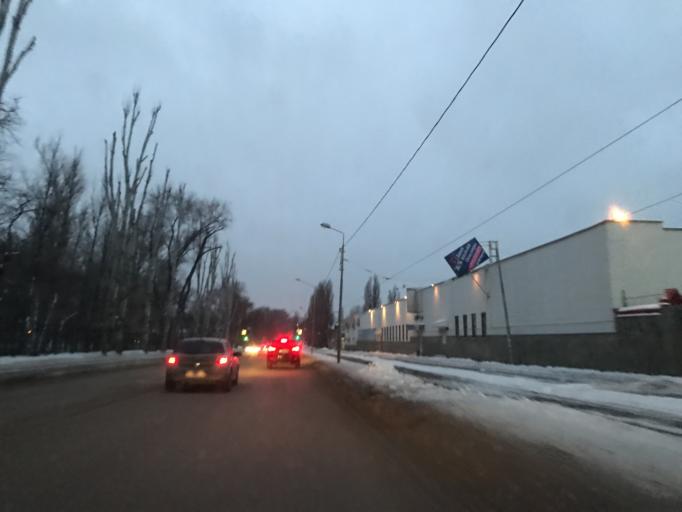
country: RU
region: Rostov
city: Imeni Chkalova
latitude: 47.2488
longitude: 39.7606
